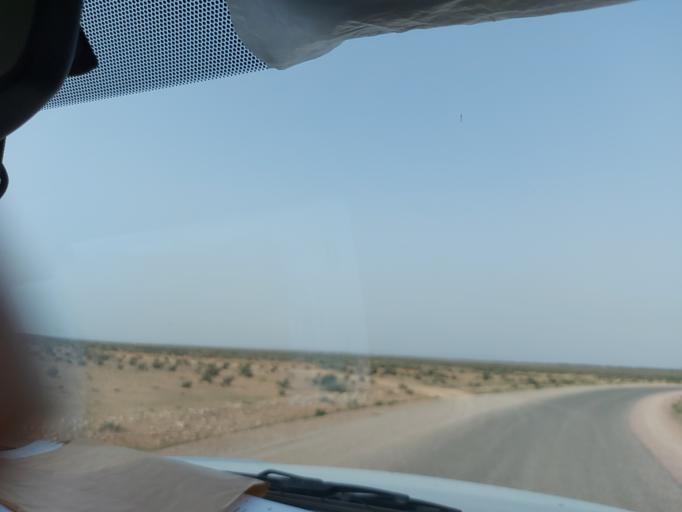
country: TN
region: Madanin
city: Medenine
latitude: 33.2861
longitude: 10.5972
